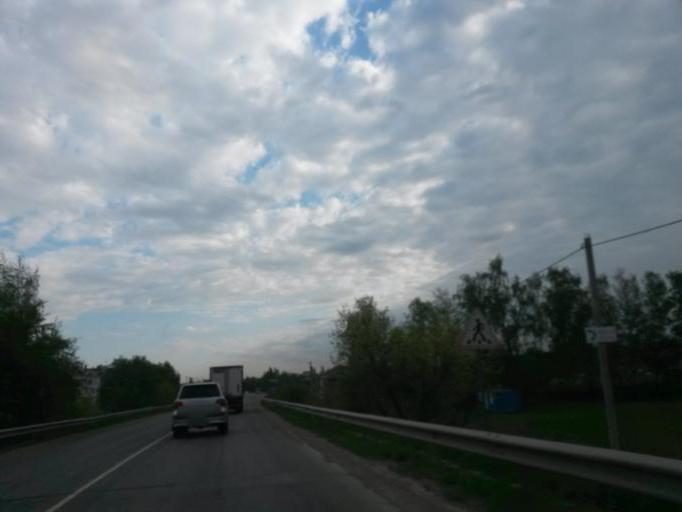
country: RU
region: Moskovskaya
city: Gorki-Leninskiye
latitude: 55.5048
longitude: 37.7809
